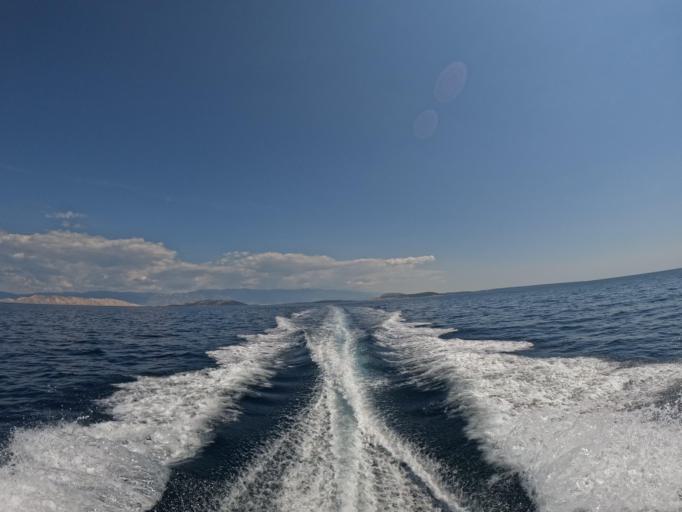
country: HR
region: Primorsko-Goranska
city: Lopar
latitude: 44.8887
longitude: 14.6366
